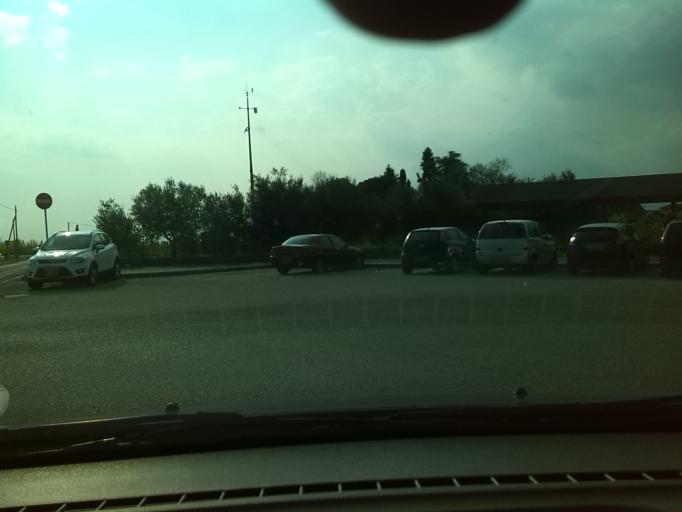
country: IT
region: Friuli Venezia Giulia
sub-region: Provincia di Udine
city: Cividale del Friuli
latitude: 46.0967
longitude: 13.4187
